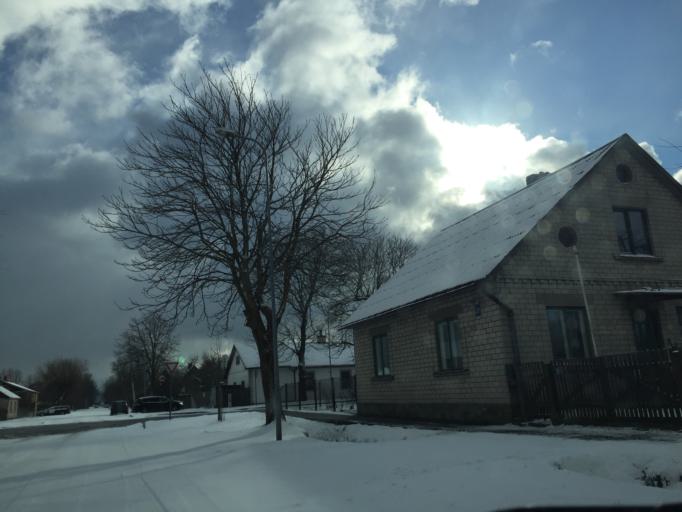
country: LV
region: Ventspils
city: Ventspils
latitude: 57.3826
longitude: 21.5621
